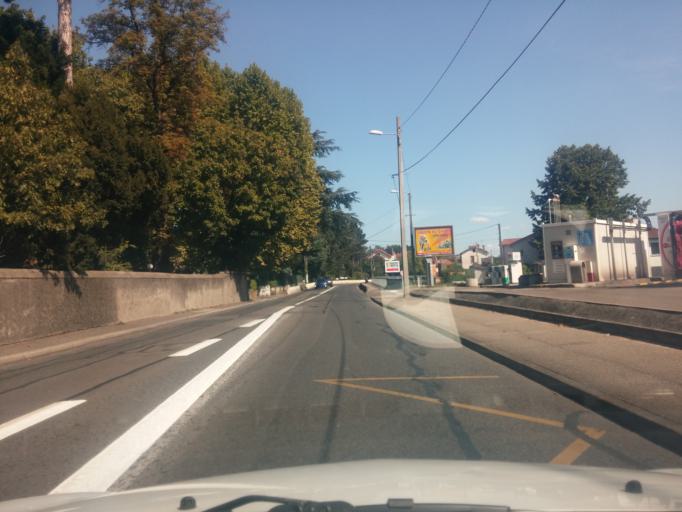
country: FR
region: Rhone-Alpes
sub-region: Departement du Rhone
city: Oullins
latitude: 45.7214
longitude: 4.7949
